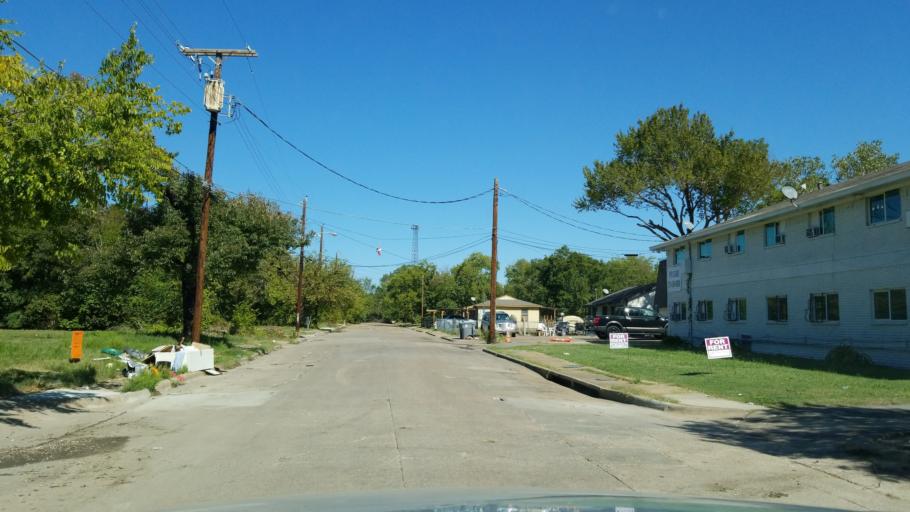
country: US
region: Texas
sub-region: Dallas County
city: Dallas
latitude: 32.7780
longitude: -96.7464
